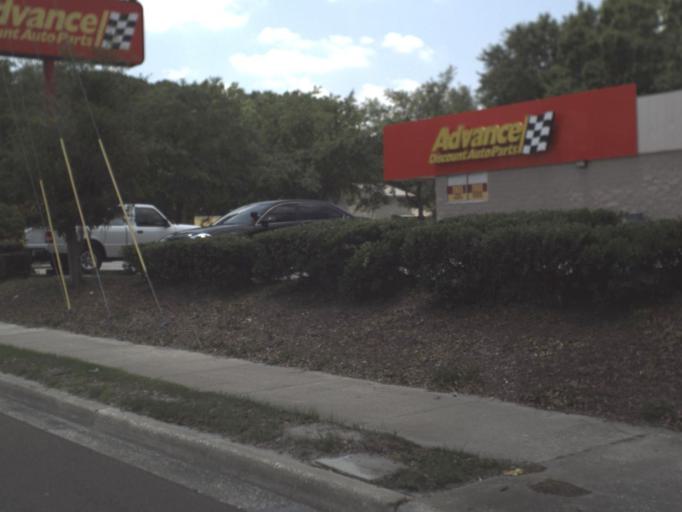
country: US
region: Florida
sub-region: Duval County
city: Jacksonville
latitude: 30.3076
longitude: -81.7307
